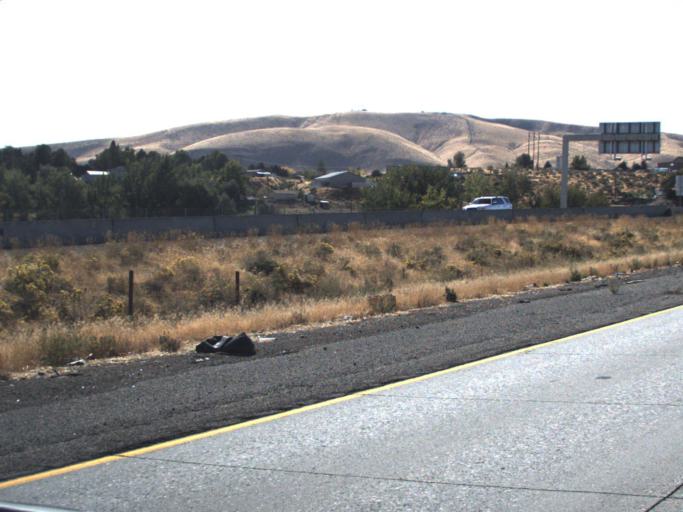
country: US
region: Washington
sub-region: Benton County
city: Richland
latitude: 46.2583
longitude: -119.2925
